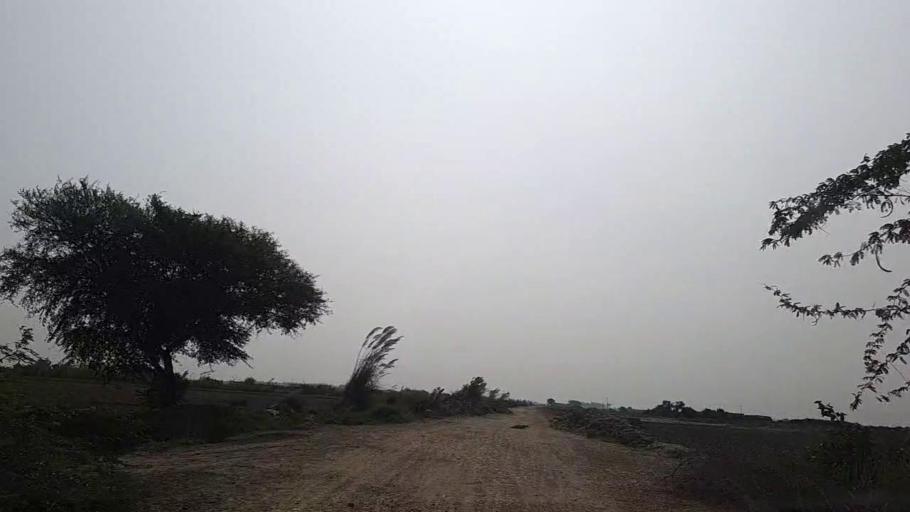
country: PK
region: Sindh
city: Mirpur Sakro
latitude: 24.6339
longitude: 67.7674
